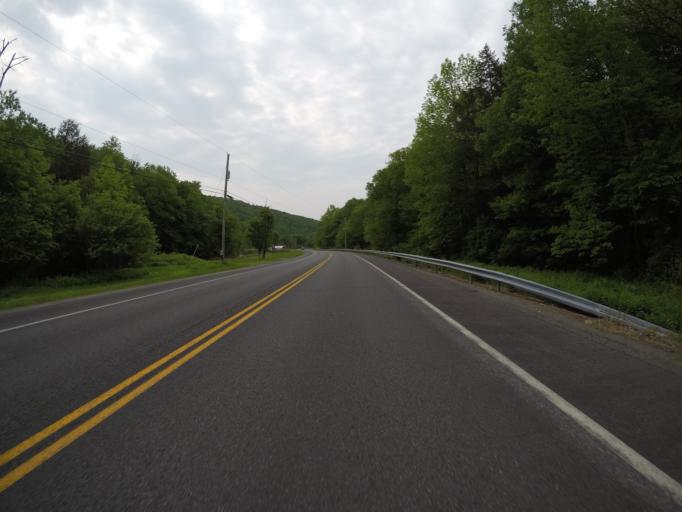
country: US
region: New York
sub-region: Sullivan County
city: Livingston Manor
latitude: 41.9827
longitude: -74.8946
